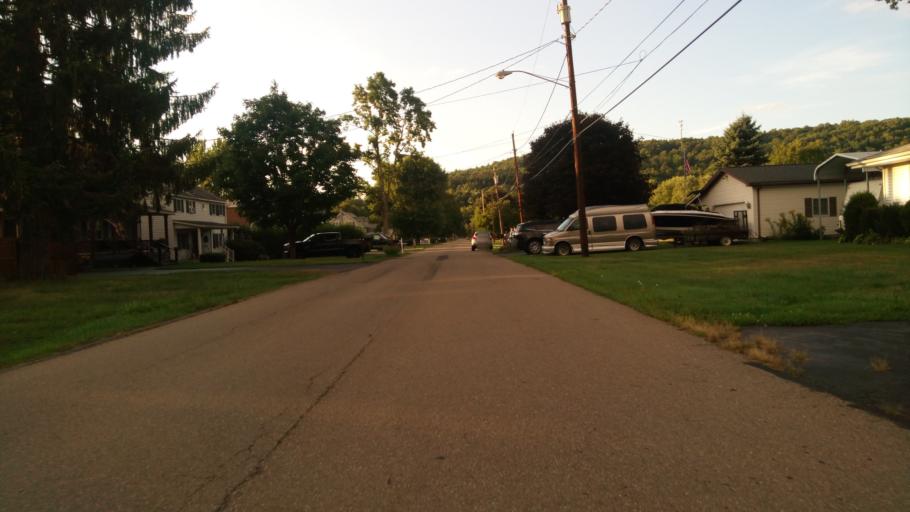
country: US
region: New York
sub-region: Chemung County
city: Southport
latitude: 42.0538
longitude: -76.8276
